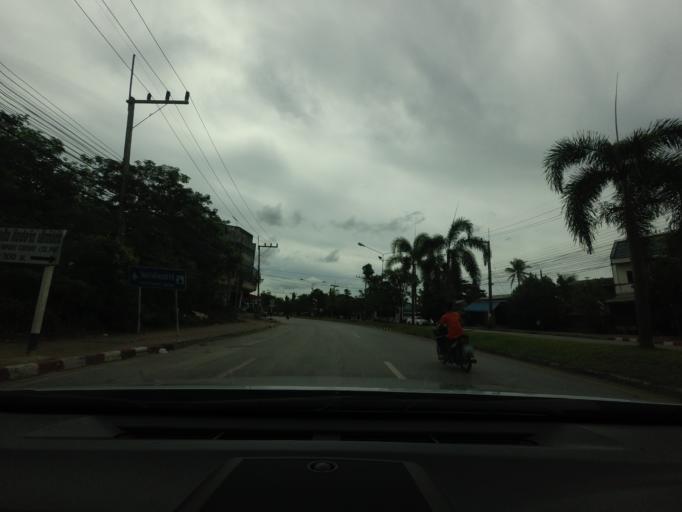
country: TH
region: Songkhla
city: Sadao
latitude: 6.6642
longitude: 100.3291
